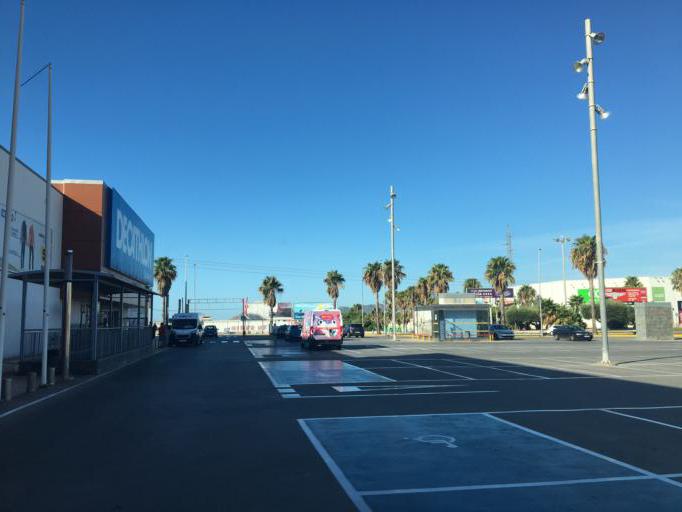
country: ES
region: Murcia
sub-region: Murcia
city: Cartagena
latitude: 37.6234
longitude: -0.9495
